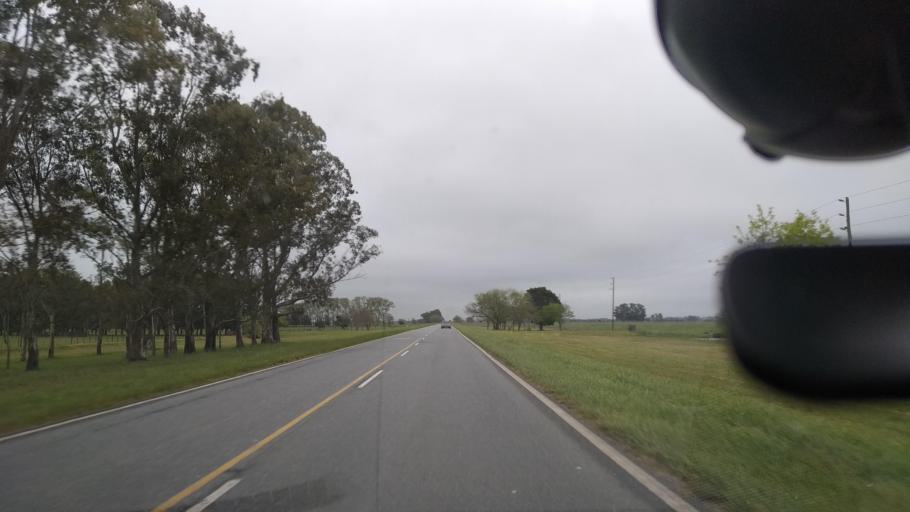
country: AR
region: Buenos Aires
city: Veronica
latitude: -35.3013
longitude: -57.5079
